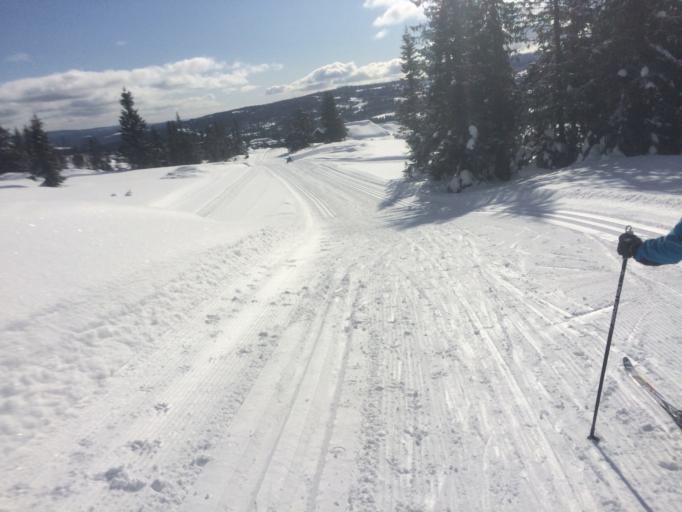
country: NO
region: Oppland
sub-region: Gausdal
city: Segalstad bru
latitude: 61.3443
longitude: 10.0753
